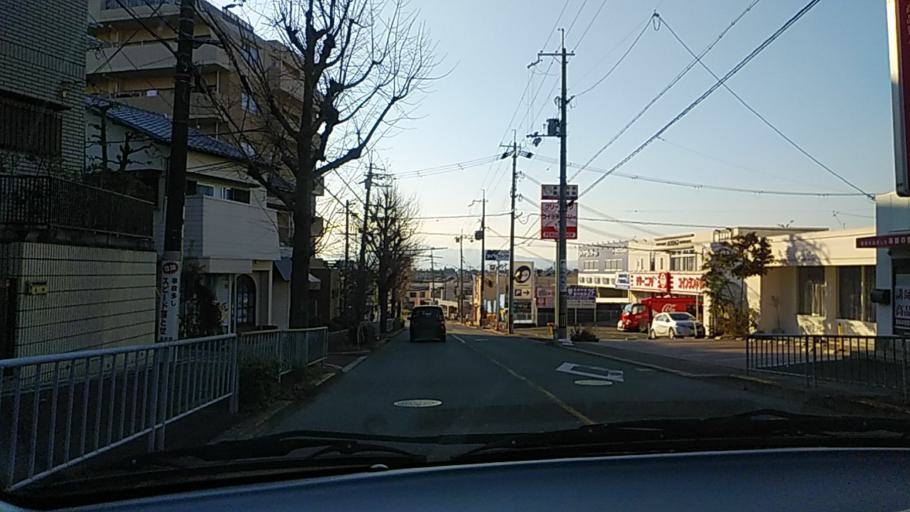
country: JP
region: Osaka
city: Toyonaka
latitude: 34.7982
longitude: 135.4851
